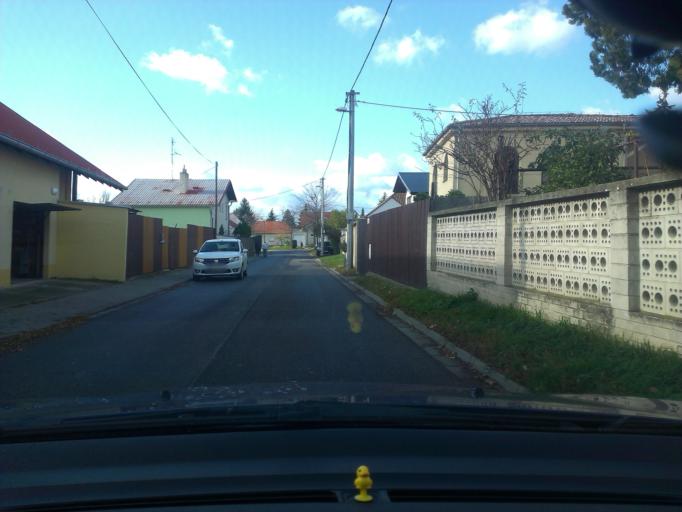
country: SK
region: Trnavsky
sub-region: Okres Trnava
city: Piestany
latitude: 48.5994
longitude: 17.8303
